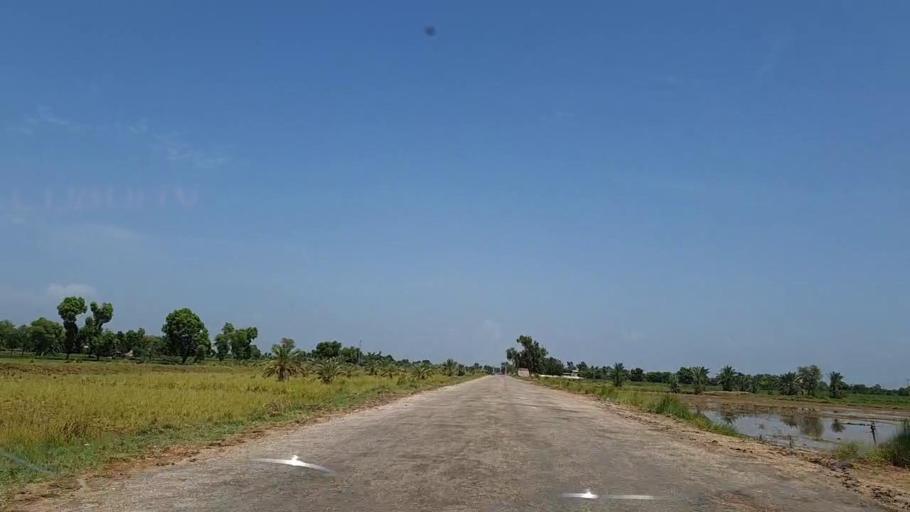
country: PK
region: Sindh
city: Naushahro Firoz
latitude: 26.8143
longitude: 68.1866
